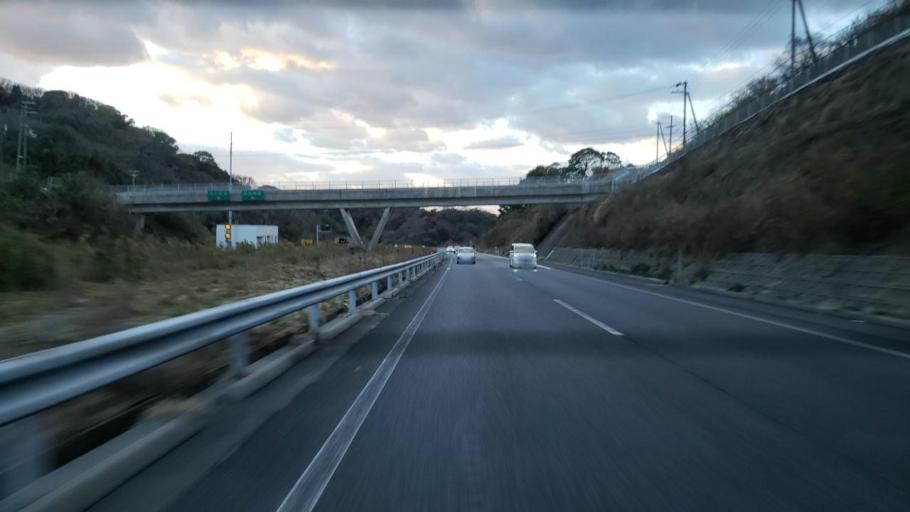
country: JP
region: Hyogo
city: Akashi
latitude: 34.5294
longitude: 134.9366
